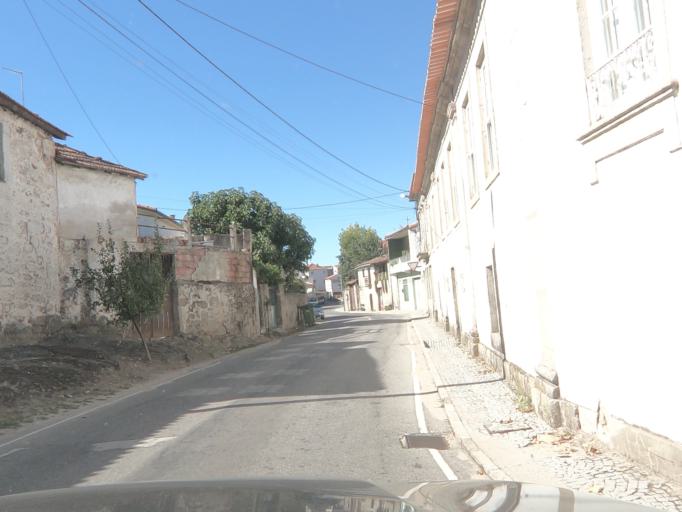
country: PT
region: Vila Real
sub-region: Valpacos
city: Valpacos
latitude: 41.6619
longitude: -7.3196
